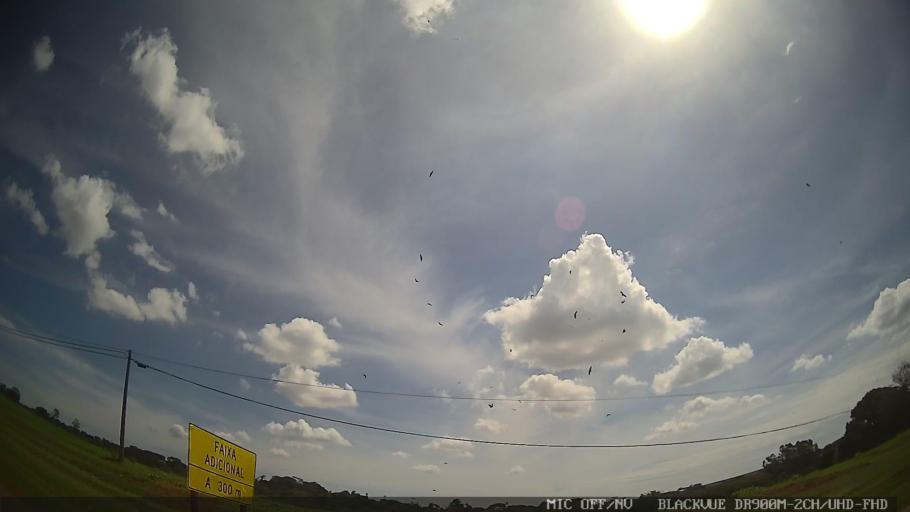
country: BR
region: Sao Paulo
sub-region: Artur Nogueira
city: Artur Nogueira
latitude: -22.6038
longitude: -47.0985
